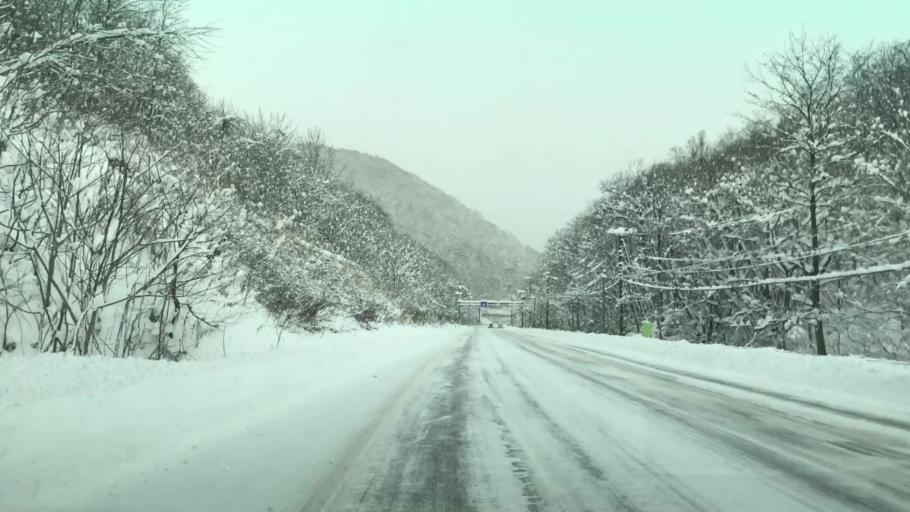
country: JP
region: Hokkaido
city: Yoichi
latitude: 43.2254
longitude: 140.7345
